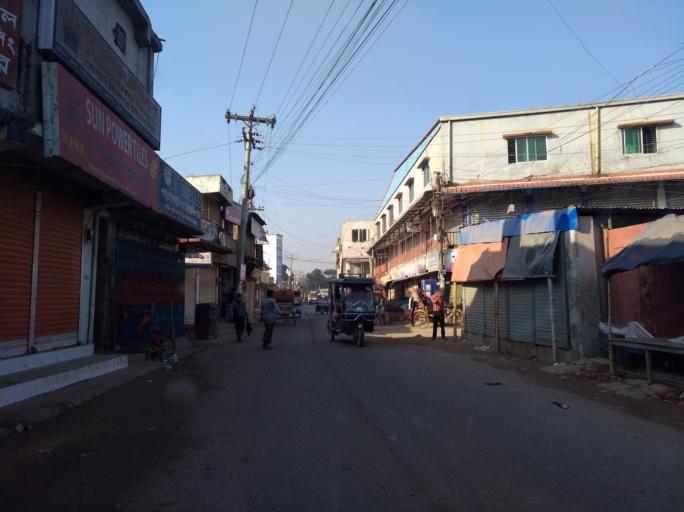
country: BD
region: Dhaka
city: Tungi
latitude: 23.9104
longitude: 90.2986
